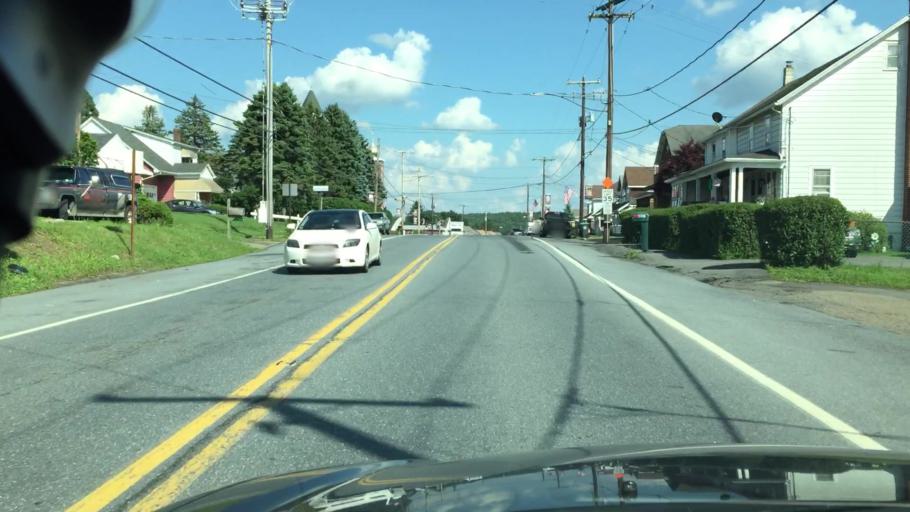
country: US
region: Pennsylvania
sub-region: Luzerne County
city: Hazleton
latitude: 40.9315
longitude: -75.9214
